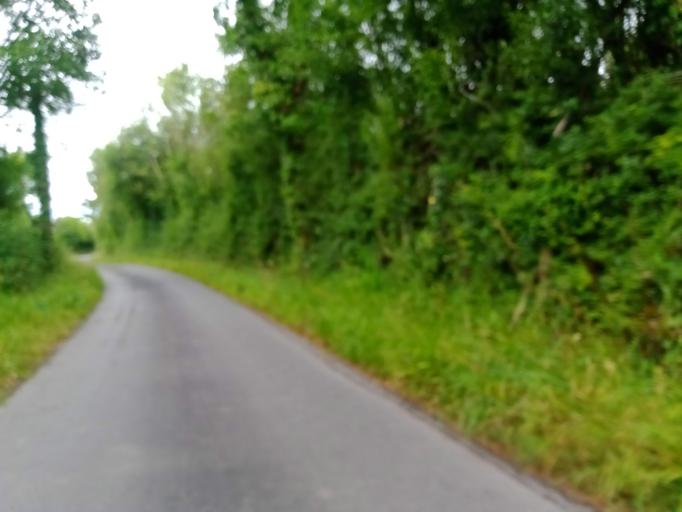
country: IE
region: Leinster
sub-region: Kilkenny
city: Callan
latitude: 52.5774
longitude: -7.4053
